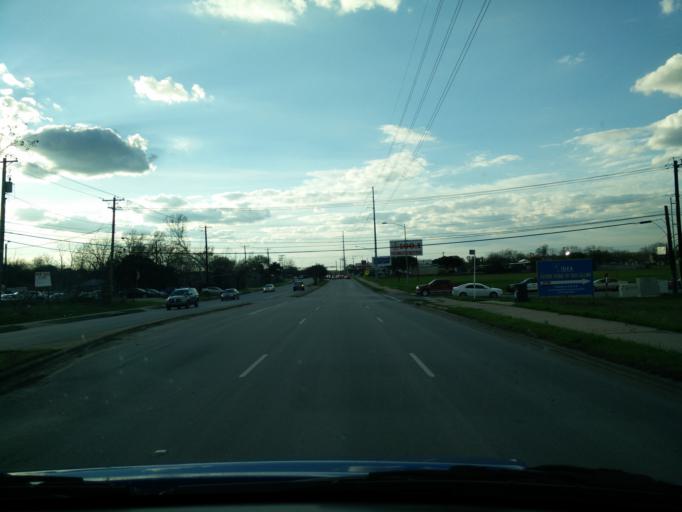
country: US
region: Texas
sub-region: Travis County
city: Austin
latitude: 30.2238
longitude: -97.7006
